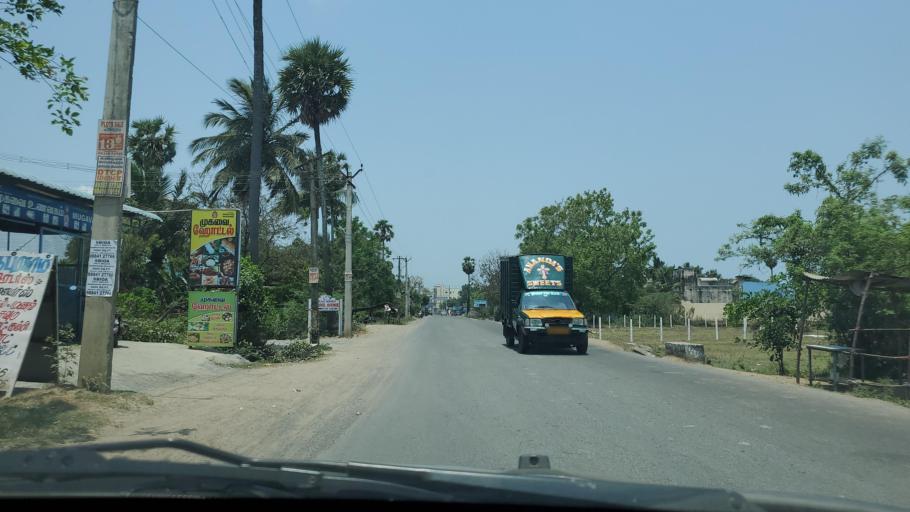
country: IN
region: Tamil Nadu
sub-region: Kancheepuram
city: Vengavasal
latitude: 12.8544
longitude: 80.1715
